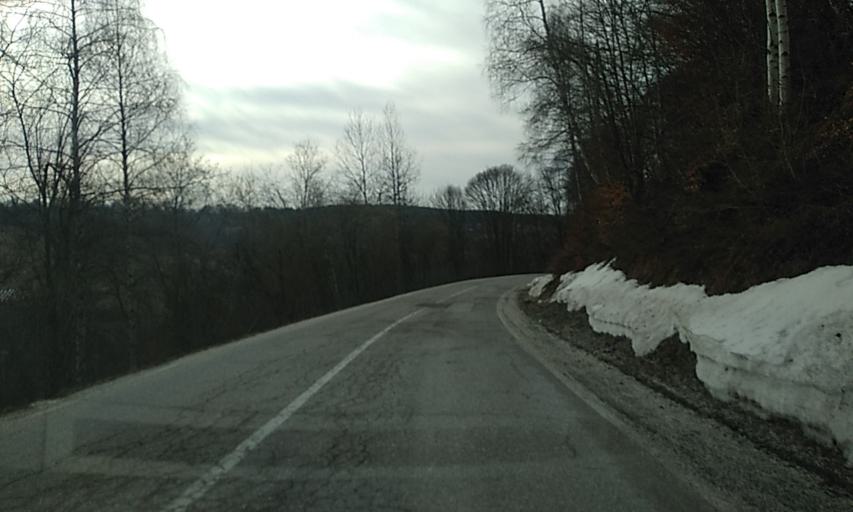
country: RS
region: Central Serbia
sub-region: Jablanicki Okrug
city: Crna Trava
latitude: 42.6625
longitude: 22.3763
